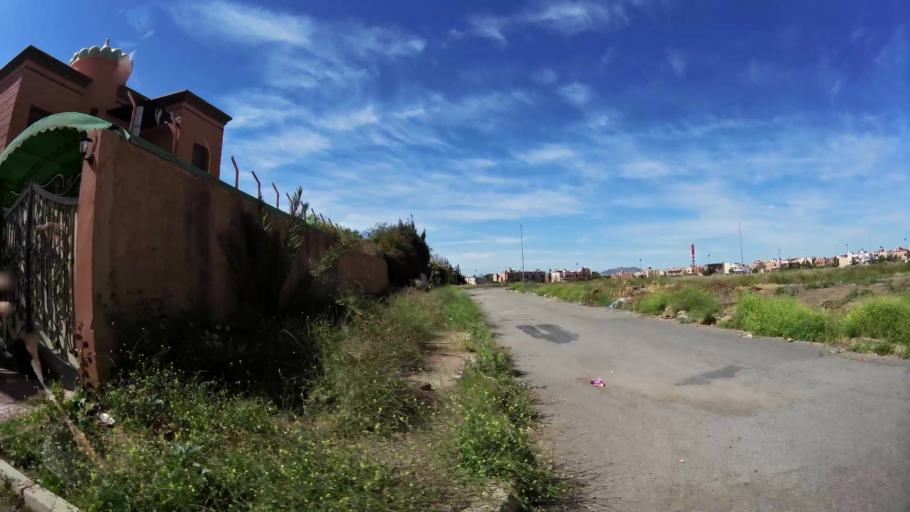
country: MA
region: Marrakech-Tensift-Al Haouz
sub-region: Marrakech
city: Marrakesh
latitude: 31.6442
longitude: -8.0452
